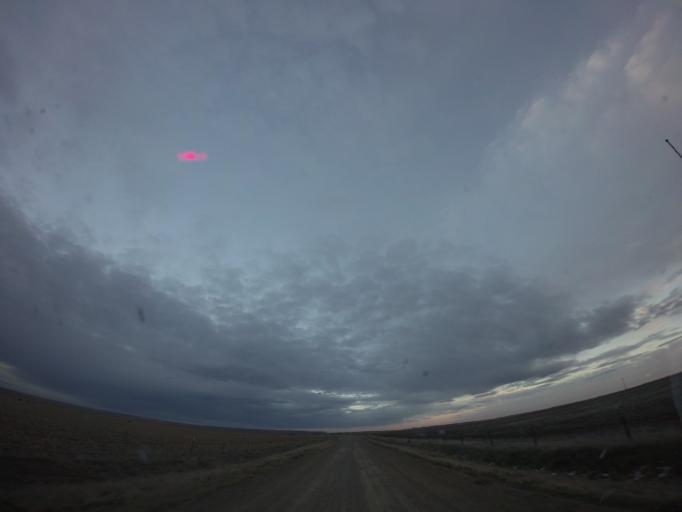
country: US
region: Montana
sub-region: Yellowstone County
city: Laurel
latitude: 45.9439
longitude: -108.7605
